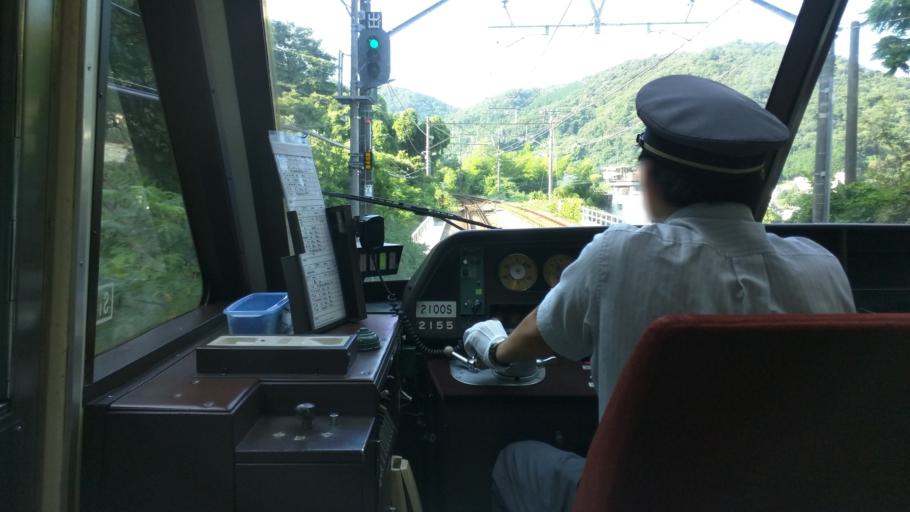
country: JP
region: Shizuoka
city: Atami
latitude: 35.0600
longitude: 139.0669
